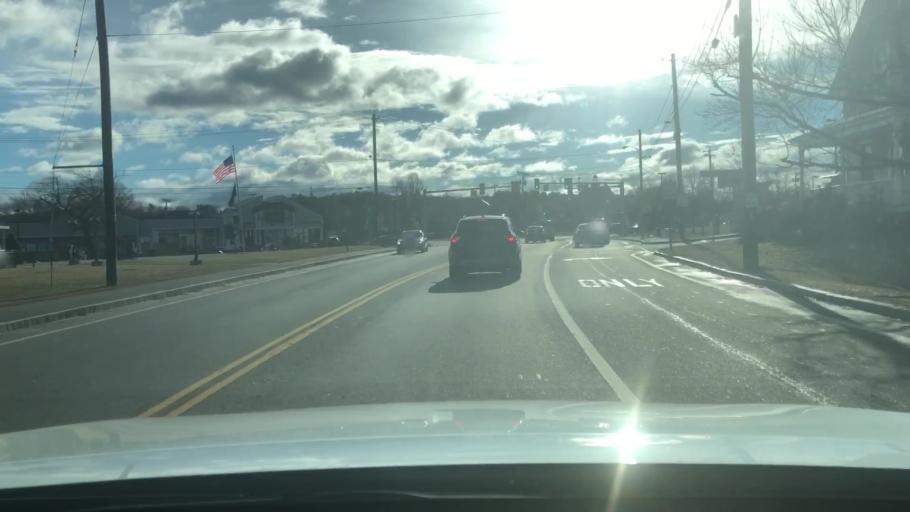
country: US
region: Rhode Island
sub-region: Providence County
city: Woonsocket
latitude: 42.0268
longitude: -71.4902
